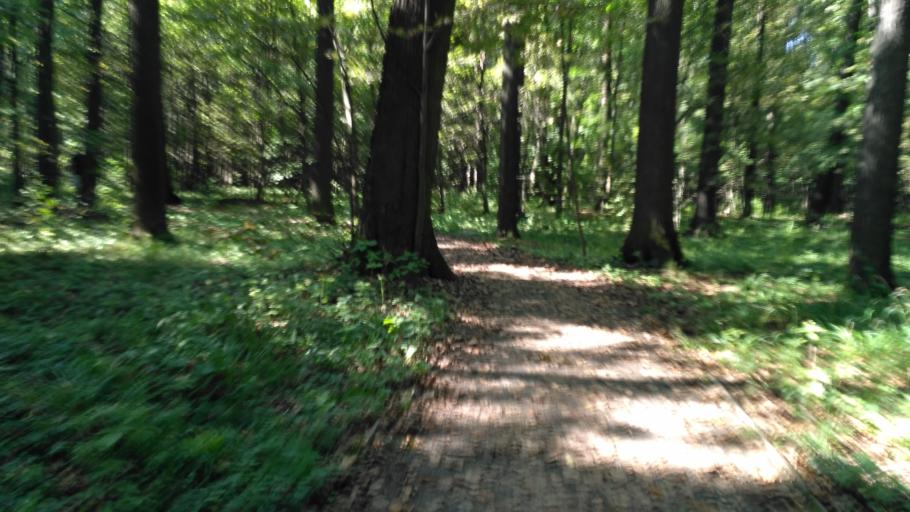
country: RU
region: Moscow
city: Ryazanskiy
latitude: 55.7701
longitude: 37.7587
